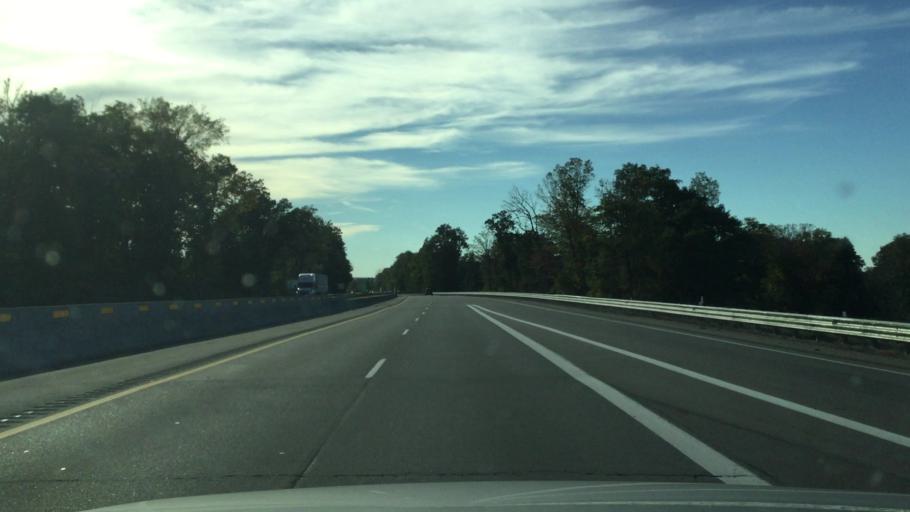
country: US
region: Michigan
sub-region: Kalamazoo County
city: Galesburg
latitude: 42.2816
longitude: -85.3804
